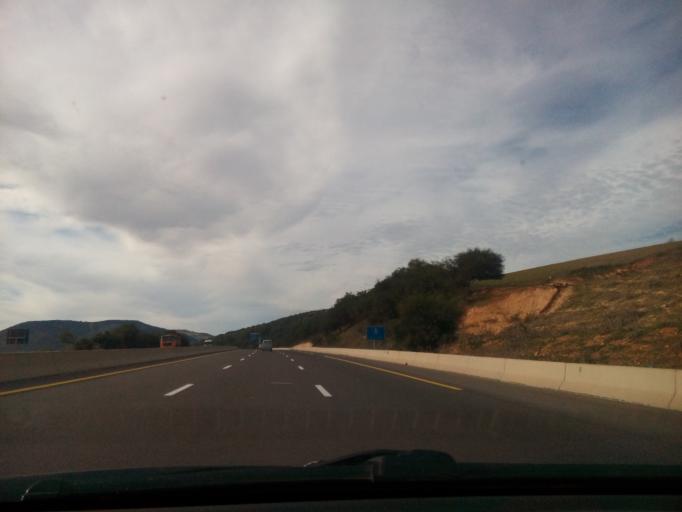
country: DZ
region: Sidi Bel Abbes
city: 'Ain el Berd
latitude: 35.4228
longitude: -0.4720
